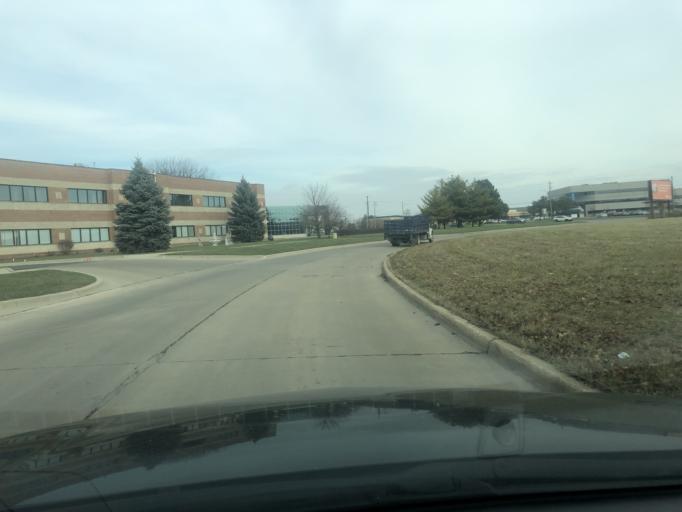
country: US
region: Michigan
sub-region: Wayne County
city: Southgate
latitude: 42.2098
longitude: -83.2308
